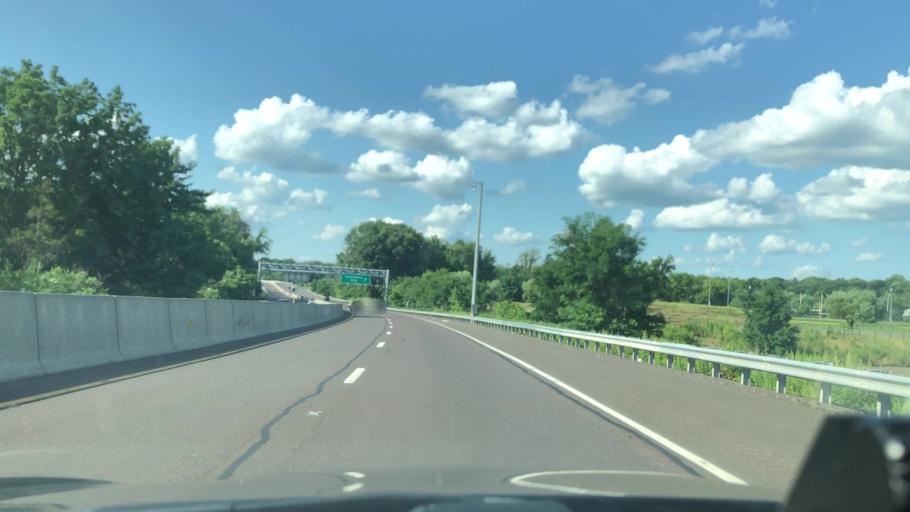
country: US
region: Pennsylvania
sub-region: Montgomery County
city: Fort Washington
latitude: 40.1549
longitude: -75.2014
